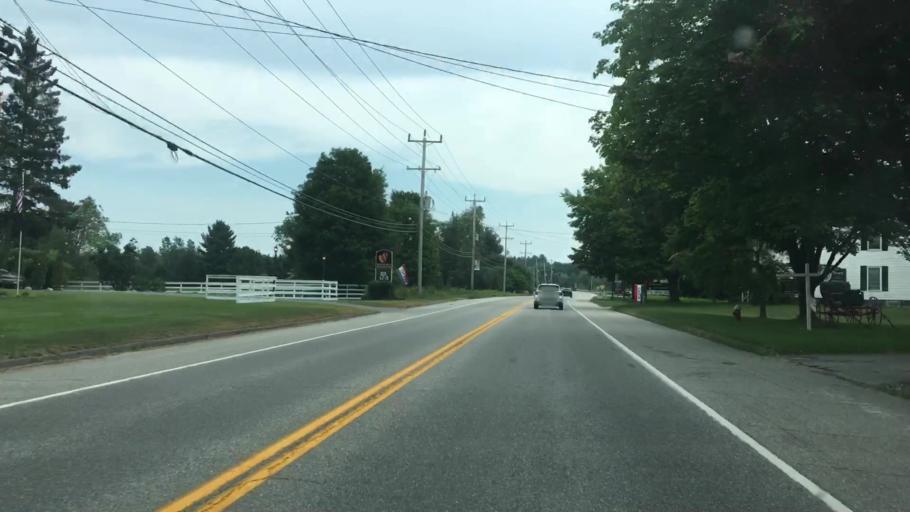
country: US
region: Maine
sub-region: Oxford County
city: Bethel
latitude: 44.4216
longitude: -70.7974
